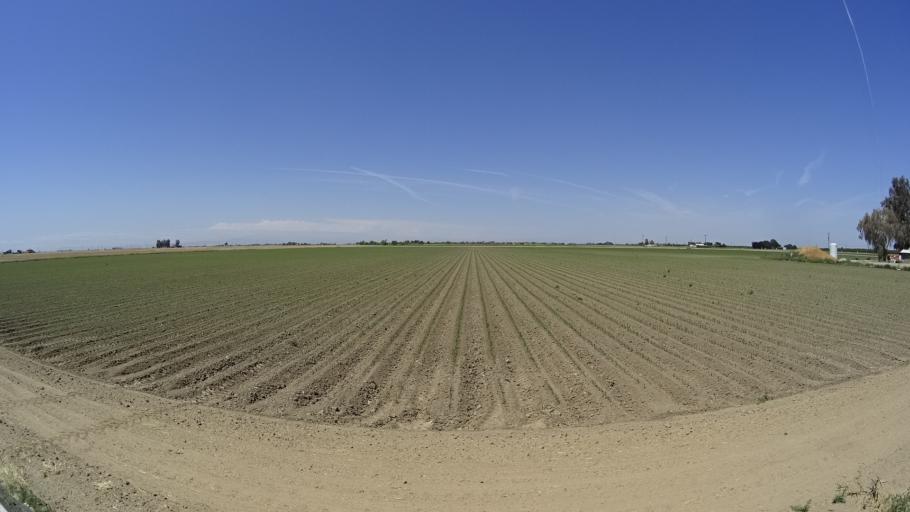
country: US
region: California
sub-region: Kings County
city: Armona
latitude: 36.2343
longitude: -119.7087
